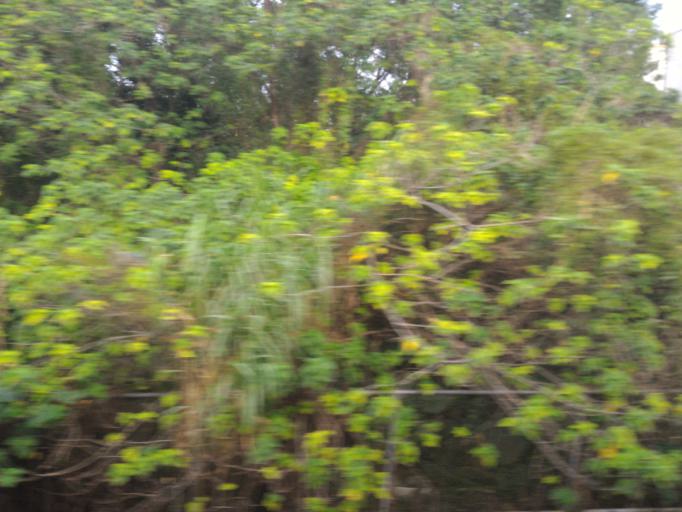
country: TW
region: Taiwan
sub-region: Taoyuan
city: Taoyuan
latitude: 24.9888
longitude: 121.3225
